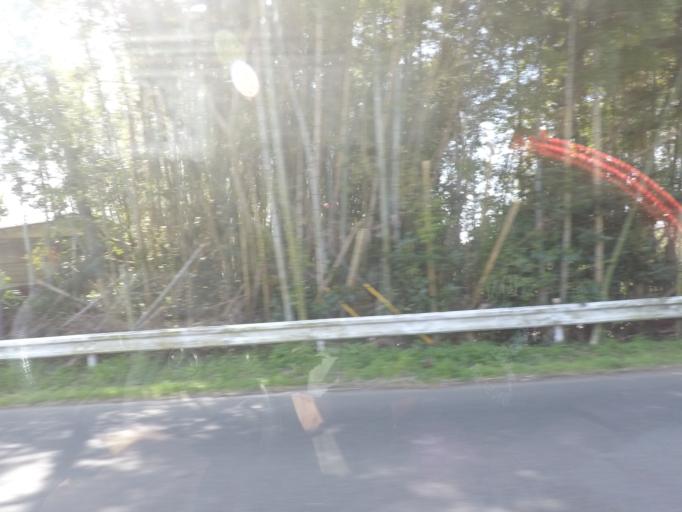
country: JP
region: Chiba
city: Narita
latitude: 35.7761
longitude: 140.3513
